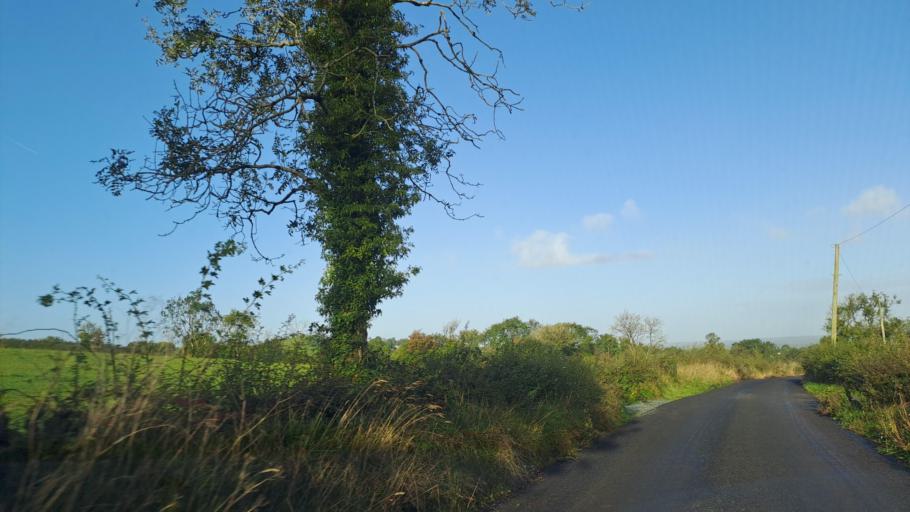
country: IE
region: Ulster
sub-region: County Monaghan
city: Castleblayney
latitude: 54.0976
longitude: -6.8846
